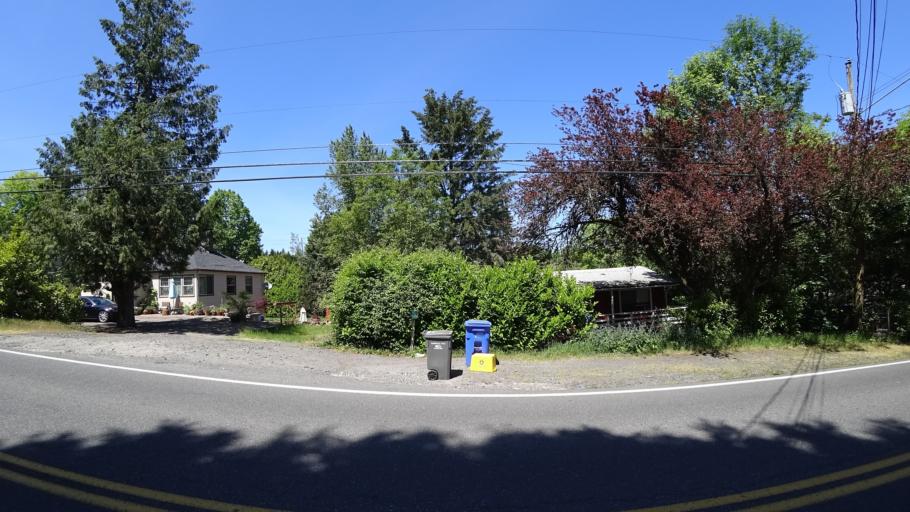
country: US
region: Oregon
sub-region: Washington County
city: Metzger
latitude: 45.4522
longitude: -122.7201
